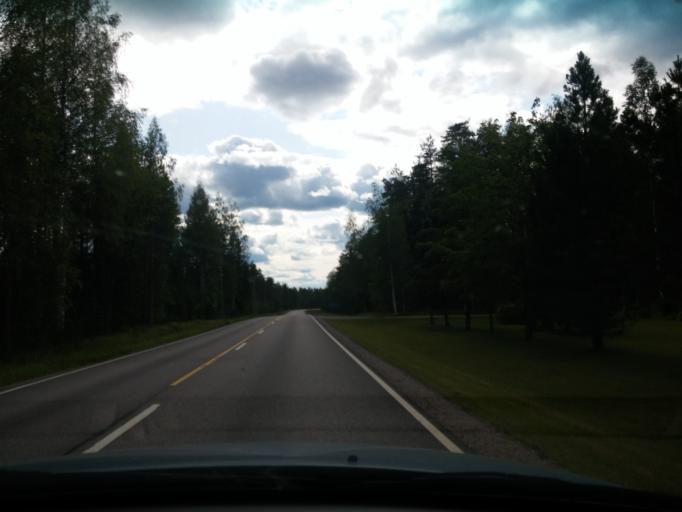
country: FI
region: Central Finland
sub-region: Saarijaervi-Viitasaari
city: Pylkoenmaeki
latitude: 62.6240
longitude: 24.7813
